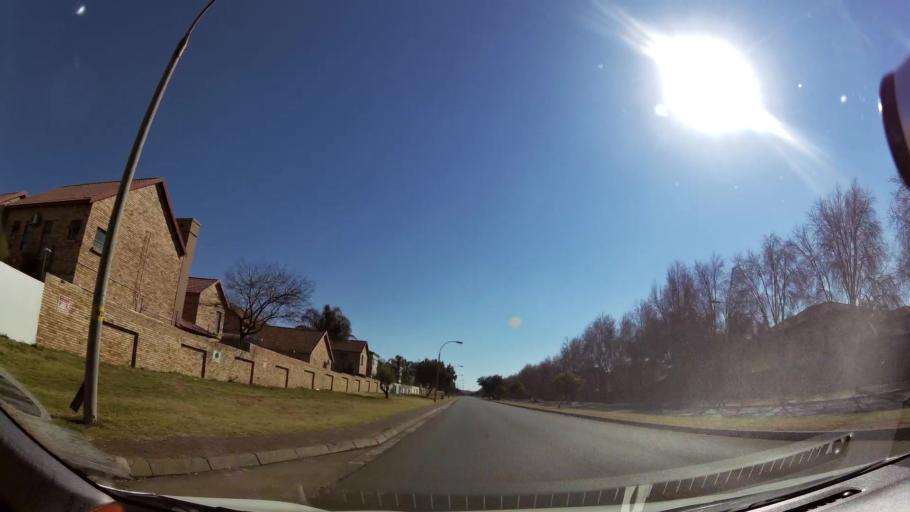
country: ZA
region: Gauteng
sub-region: Ekurhuleni Metropolitan Municipality
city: Germiston
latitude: -26.2988
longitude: 28.0936
